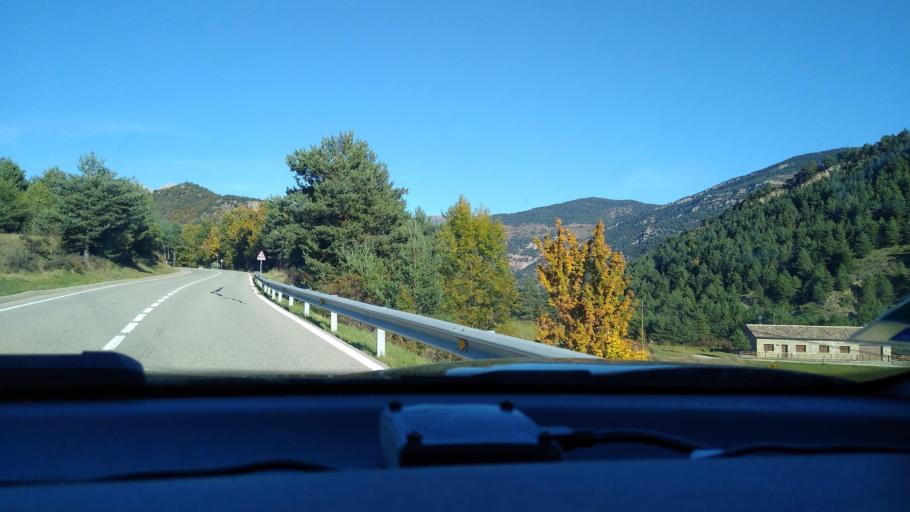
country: ES
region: Catalonia
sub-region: Provincia de Barcelona
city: Vallcebre
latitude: 42.2217
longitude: 1.8238
